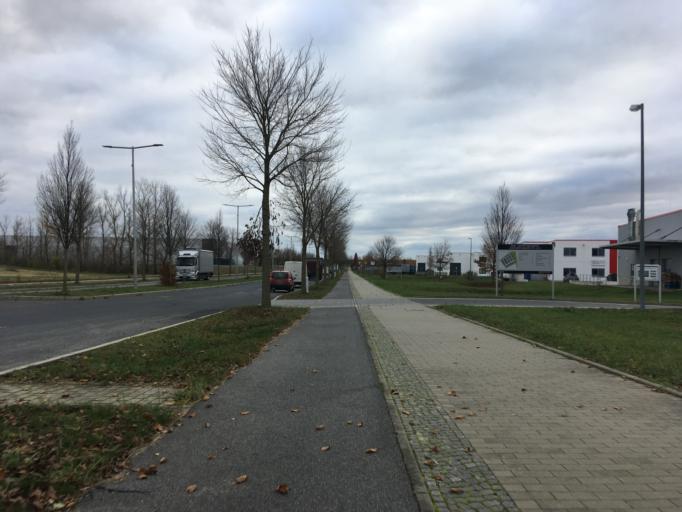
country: DE
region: Berlin
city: Altglienicke
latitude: 52.3946
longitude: 13.5428
